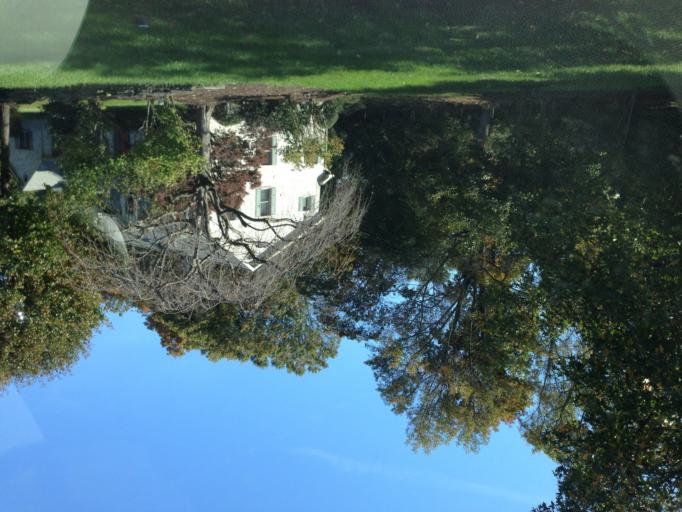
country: US
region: Maryland
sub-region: Howard County
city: Columbia
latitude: 39.2508
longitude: -76.8292
